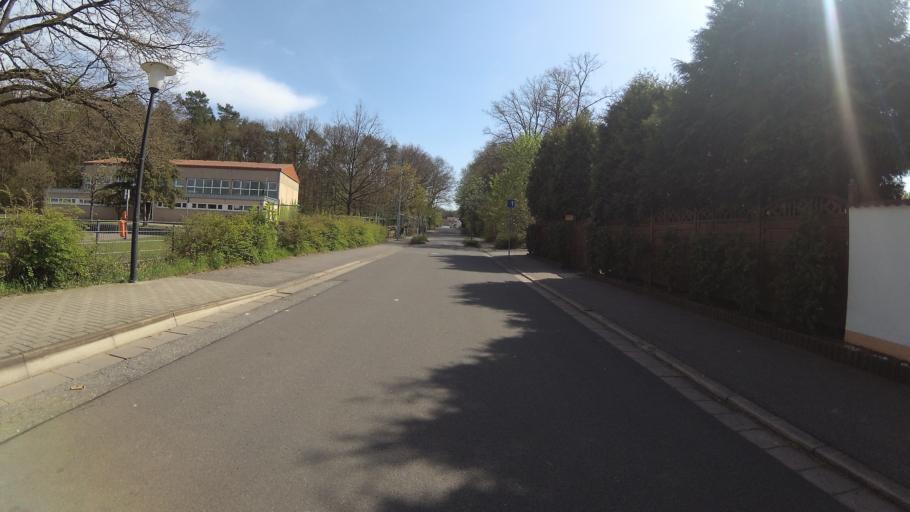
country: DE
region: Saarland
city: Homburg
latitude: 49.3443
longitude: 7.3656
